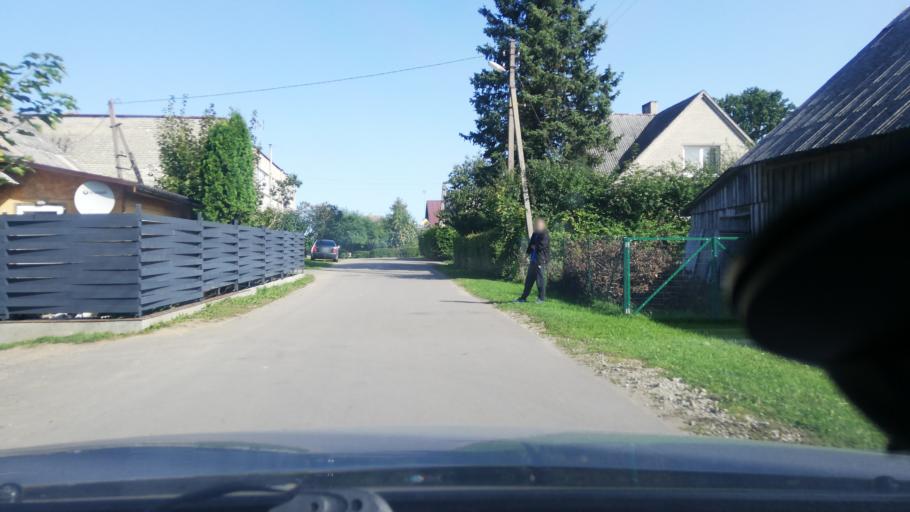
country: LT
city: Salantai
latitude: 55.9215
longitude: 21.4753
